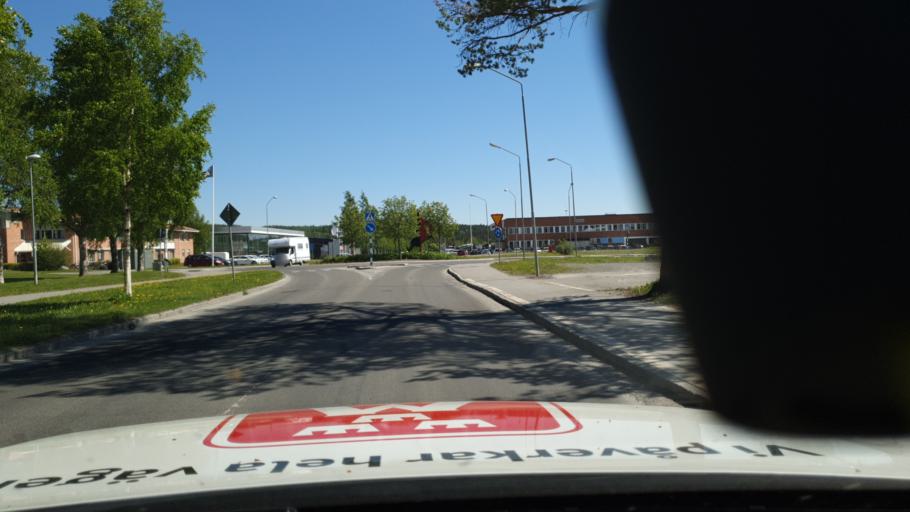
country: SE
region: Jaemtland
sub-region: OEstersunds Kommun
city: Ostersund
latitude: 63.1699
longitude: 14.6821
